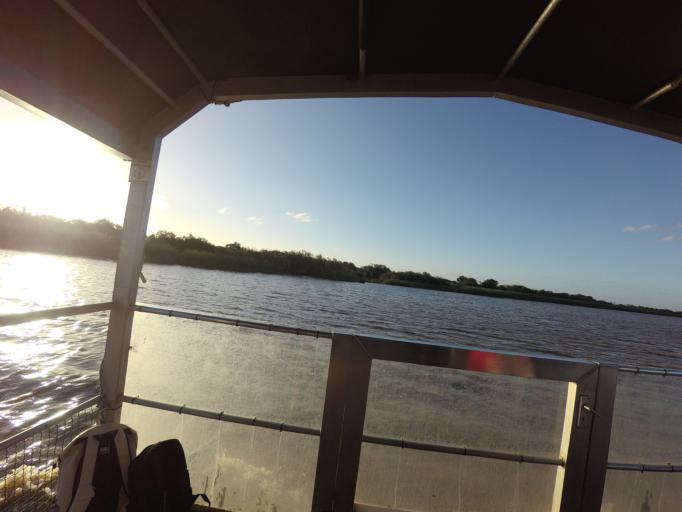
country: ZA
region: KwaZulu-Natal
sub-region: uMkhanyakude District Municipality
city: Mtubatuba
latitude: -28.3400
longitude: 32.4041
